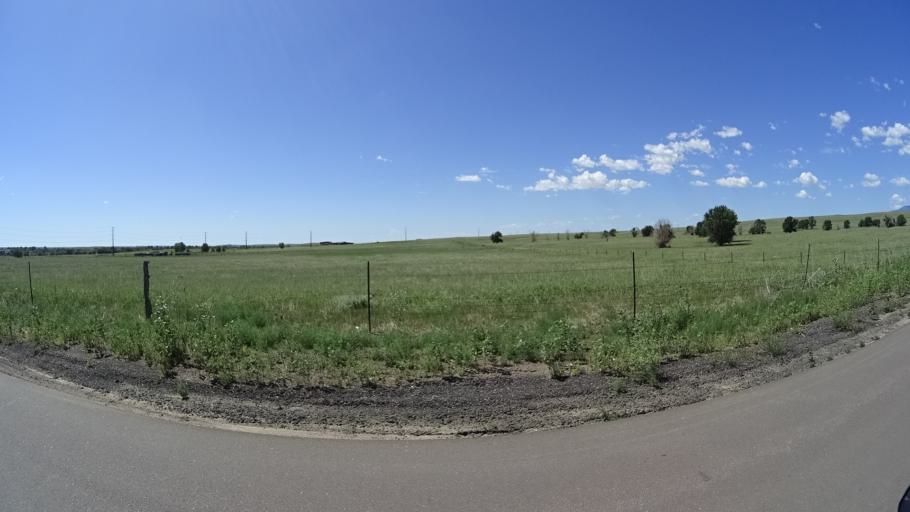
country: US
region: Colorado
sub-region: El Paso County
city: Security-Widefield
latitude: 38.7812
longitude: -104.6685
